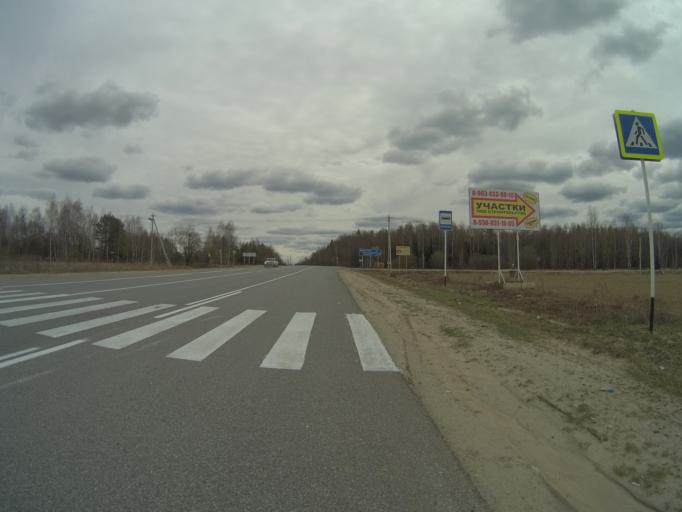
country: RU
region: Vladimir
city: Golovino
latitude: 55.9679
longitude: 40.5505
